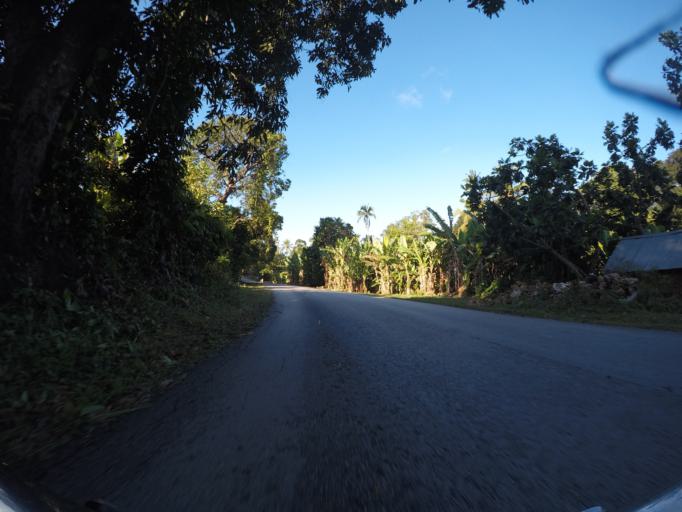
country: TZ
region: Pemba South
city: Mtambile
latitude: -5.3762
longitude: 39.6944
